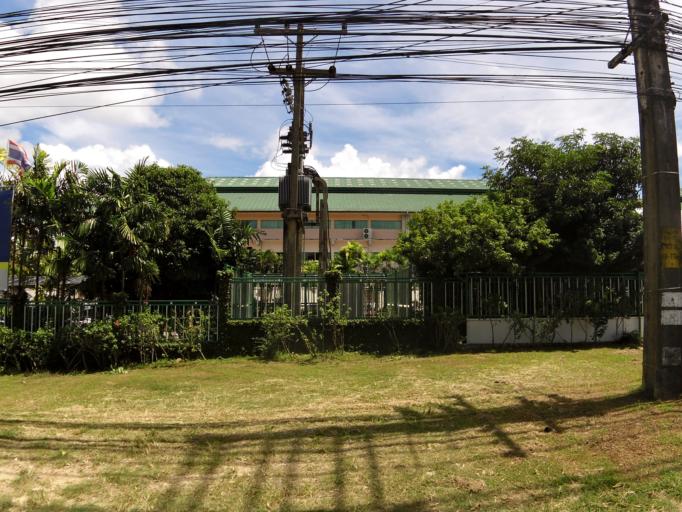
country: TH
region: Phuket
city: Mueang Phuket
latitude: 7.8709
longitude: 98.3603
